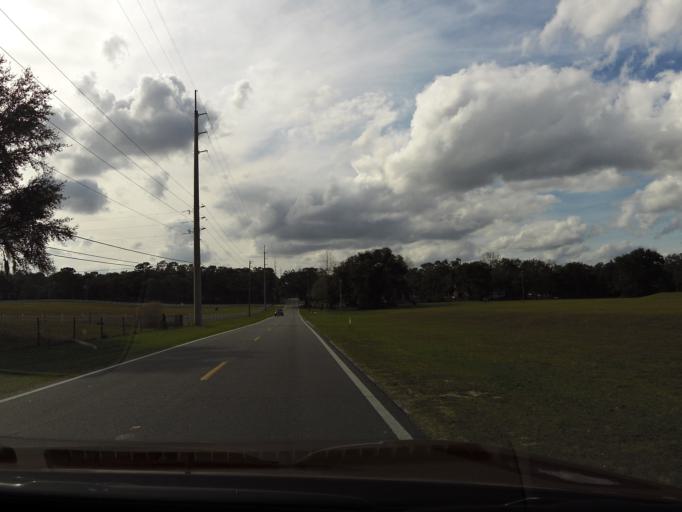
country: US
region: Florida
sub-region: Volusia County
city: De Leon Springs
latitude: 29.1370
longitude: -81.3442
